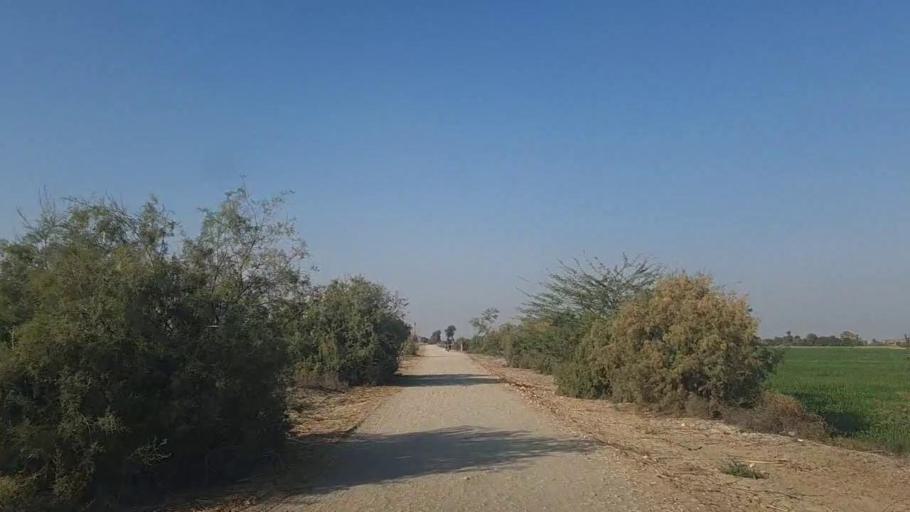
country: PK
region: Sindh
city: Jam Sahib
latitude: 26.3302
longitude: 68.7144
